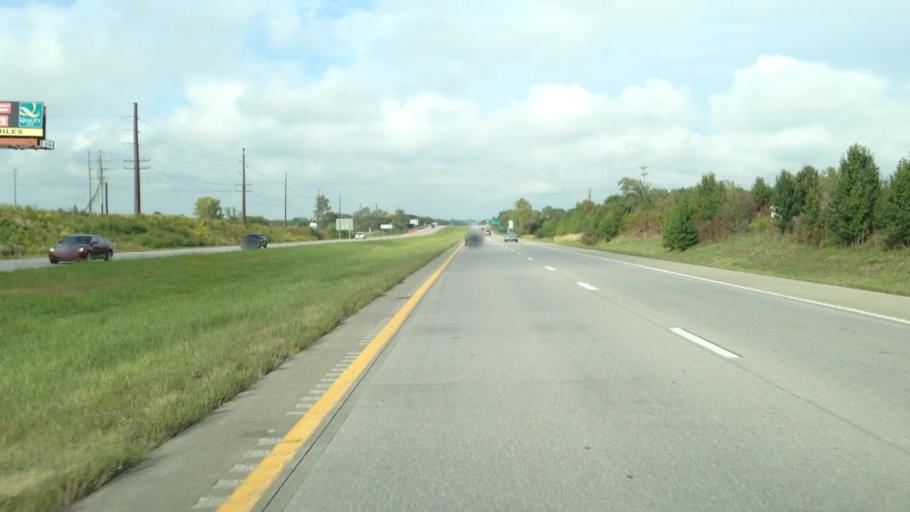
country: US
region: Missouri
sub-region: Clay County
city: Kearney
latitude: 39.3738
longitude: -94.3690
